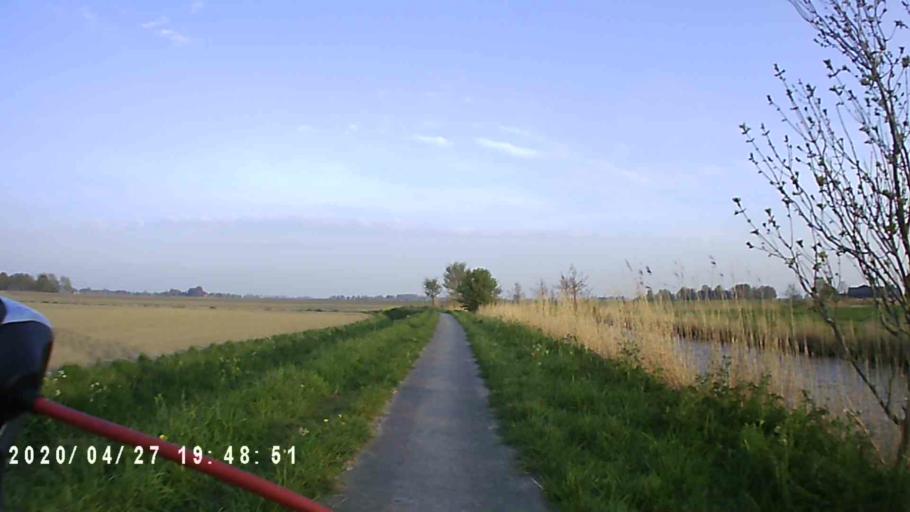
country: NL
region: Groningen
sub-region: Gemeente Zuidhorn
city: Oldehove
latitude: 53.3474
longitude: 6.4353
